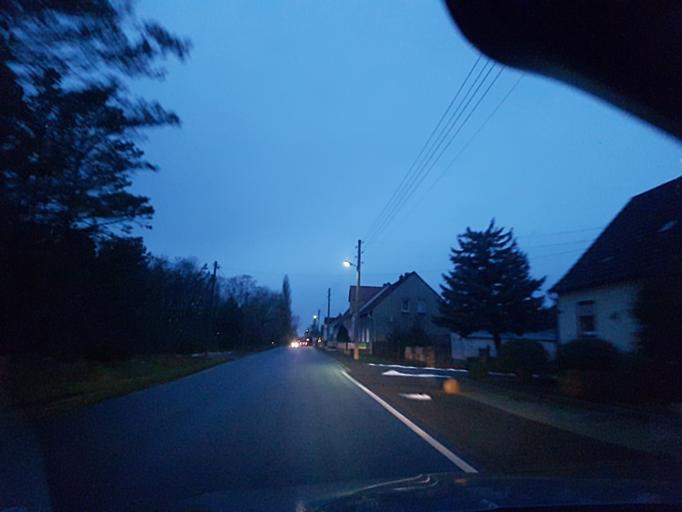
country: DE
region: Brandenburg
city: Doberlug-Kirchhain
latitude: 51.6100
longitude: 13.6037
